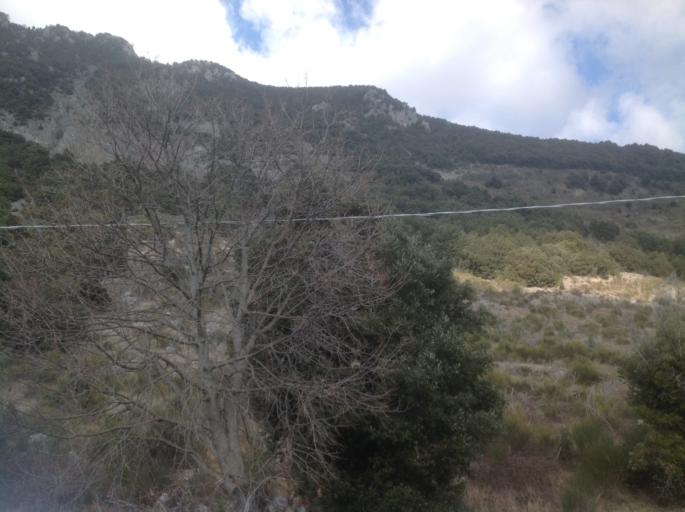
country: IT
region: Calabria
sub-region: Provincia di Cosenza
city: Civita
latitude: 39.8445
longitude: 16.3052
